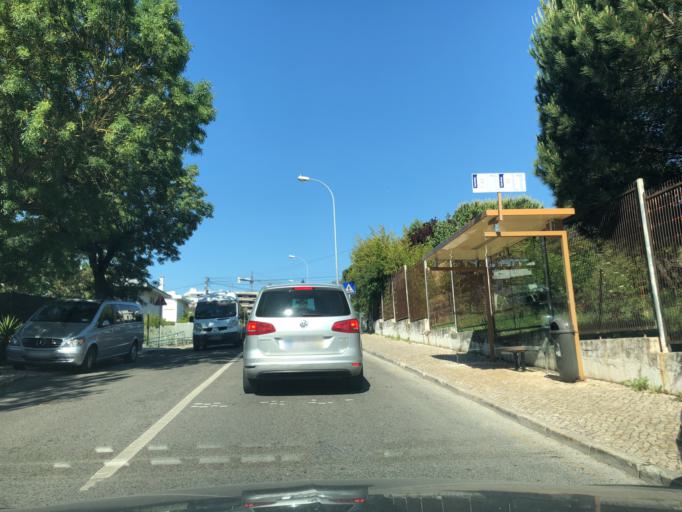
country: PT
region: Lisbon
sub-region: Oeiras
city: Paco de Arcos
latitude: 38.6976
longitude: -9.2962
